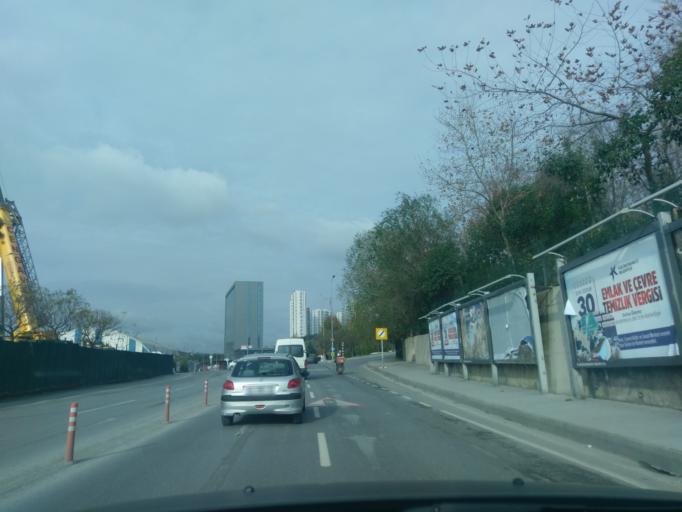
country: TR
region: Istanbul
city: Basaksehir
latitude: 41.0562
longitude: 28.7748
